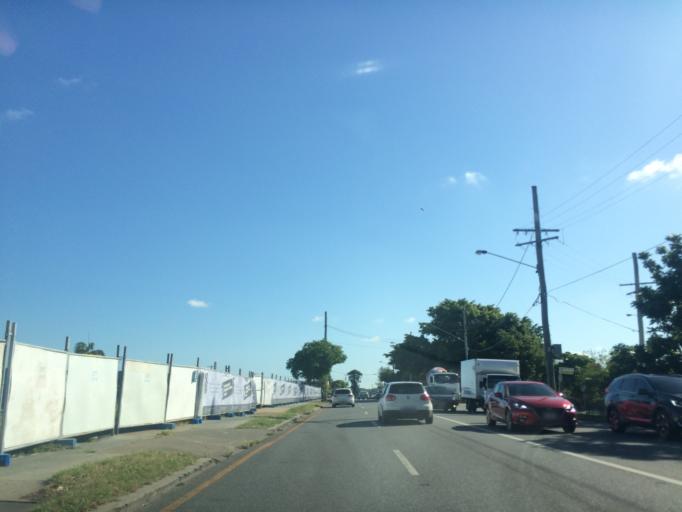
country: AU
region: Queensland
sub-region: Brisbane
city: Woolloongabba
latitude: -27.4784
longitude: 153.0477
